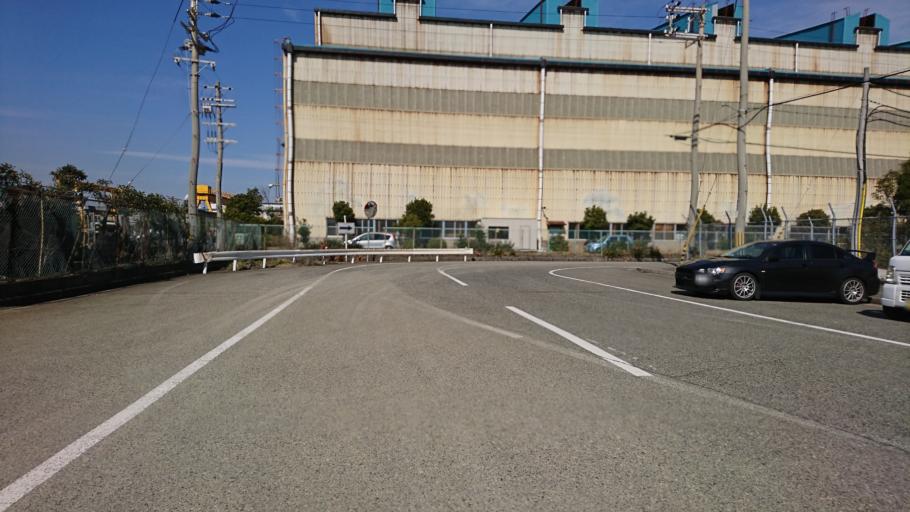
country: JP
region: Hyogo
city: Kakogawacho-honmachi
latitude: 34.6968
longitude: 134.8448
